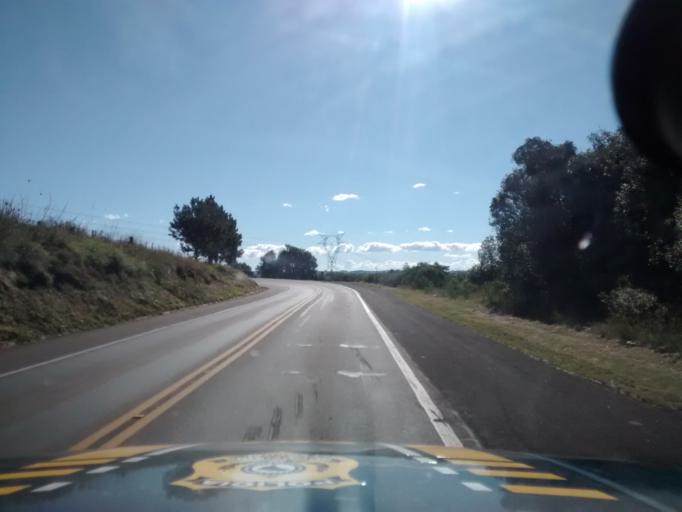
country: BR
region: Rio Grande do Sul
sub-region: Lagoa Vermelha
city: Lagoa Vermelha
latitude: -28.3340
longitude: -51.2975
